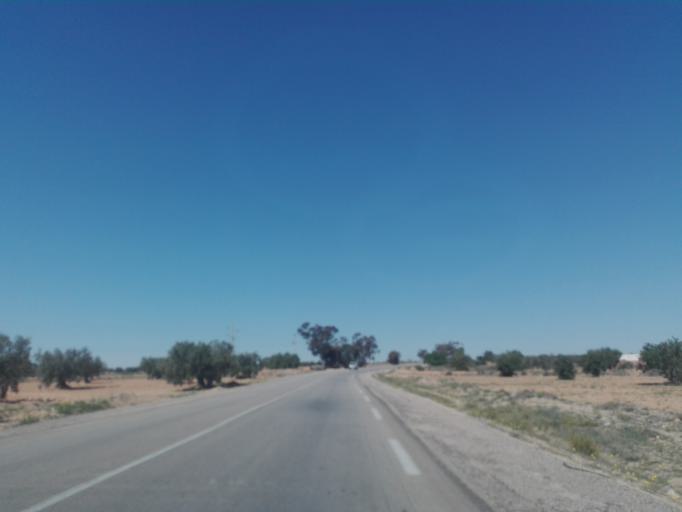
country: TN
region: Safaqis
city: Bi'r `Ali Bin Khalifah
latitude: 34.7467
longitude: 10.3571
